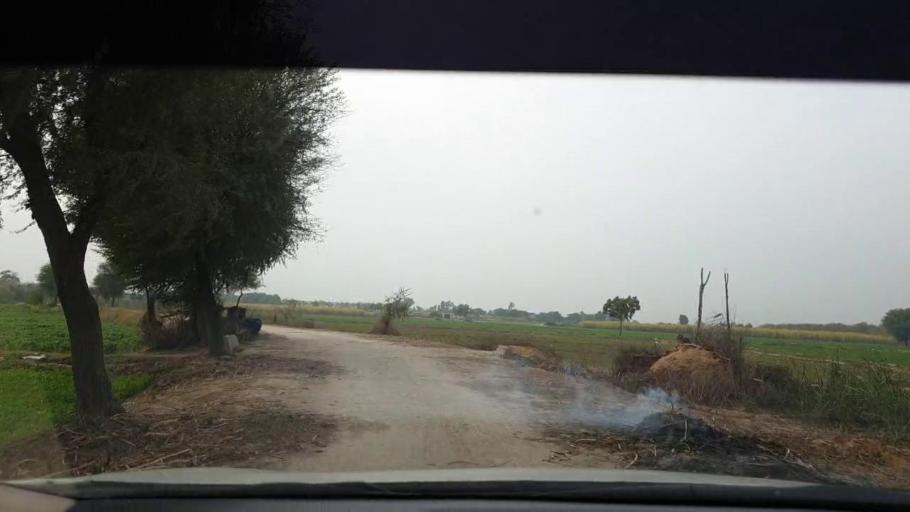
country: PK
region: Sindh
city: Berani
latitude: 25.8648
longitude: 68.7925
